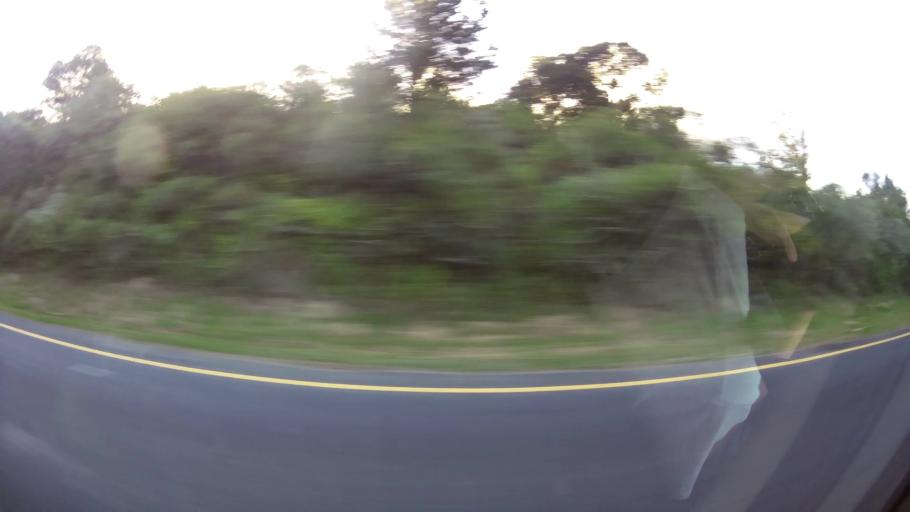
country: ZA
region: Western Cape
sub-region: Eden District Municipality
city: George
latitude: -33.9989
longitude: 22.6675
